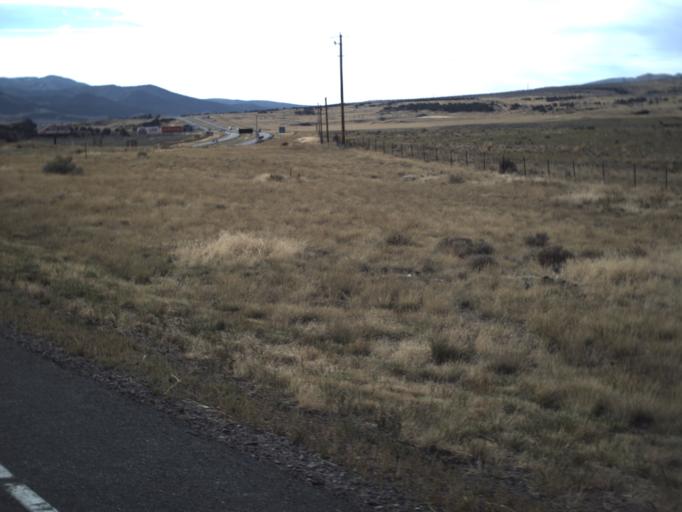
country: US
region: Utah
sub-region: Beaver County
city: Beaver
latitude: 38.6135
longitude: -112.6102
